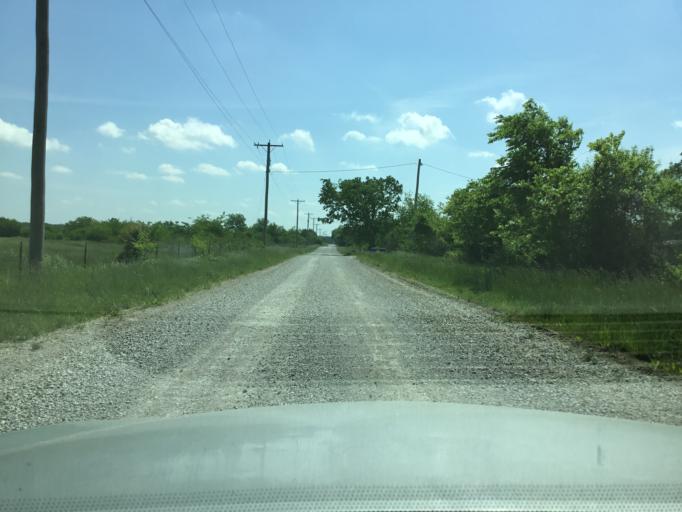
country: US
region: Kansas
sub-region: Labette County
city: Parsons
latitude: 37.3110
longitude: -95.2618
